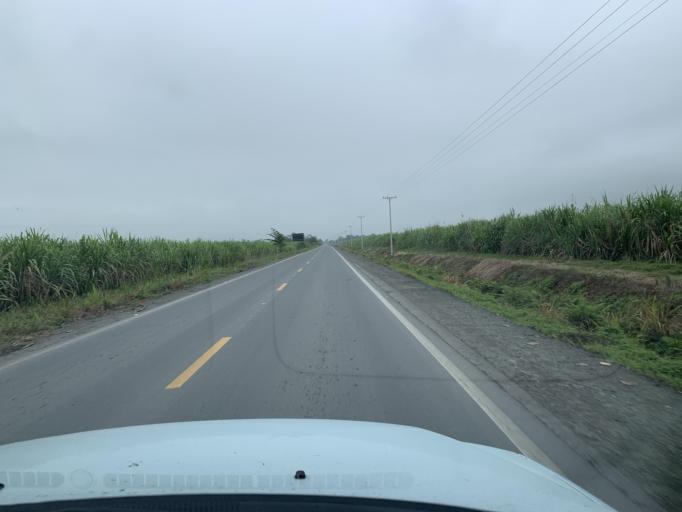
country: EC
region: Guayas
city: Coronel Marcelino Mariduena
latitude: -2.3243
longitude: -79.5211
